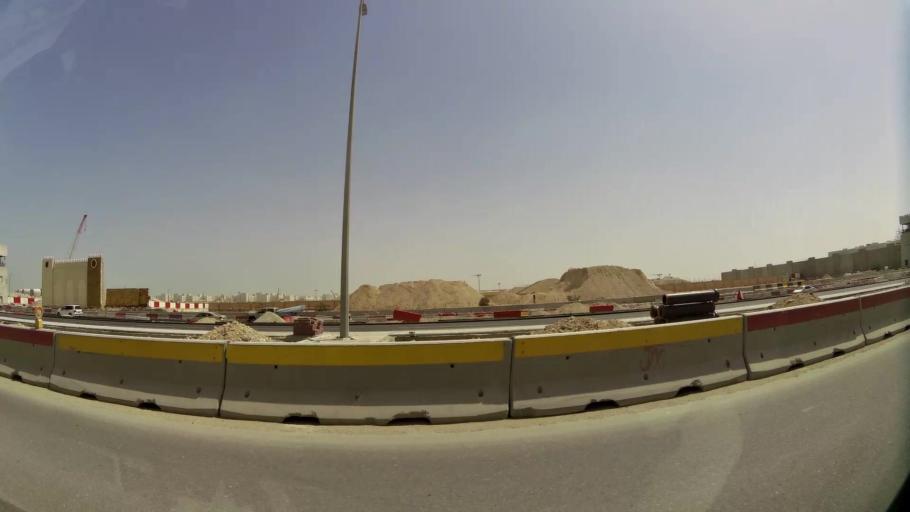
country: QA
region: Baladiyat Umm Salal
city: Umm Salal Muhammad
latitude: 25.3719
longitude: 51.4603
